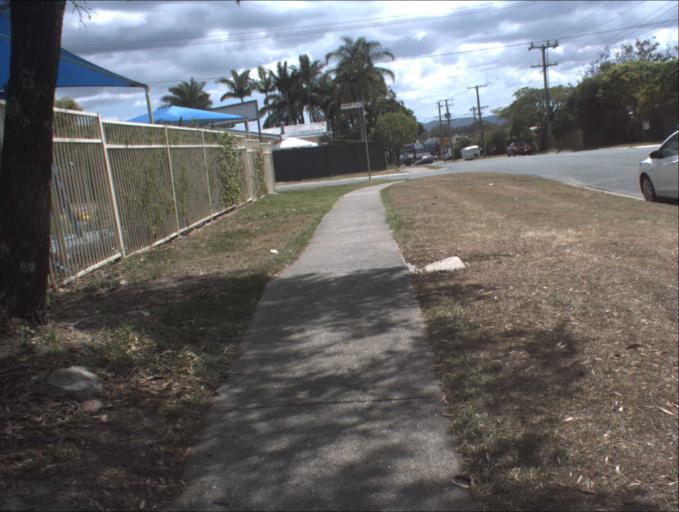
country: AU
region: Queensland
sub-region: Logan
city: Beenleigh
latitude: -27.7162
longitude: 153.1895
